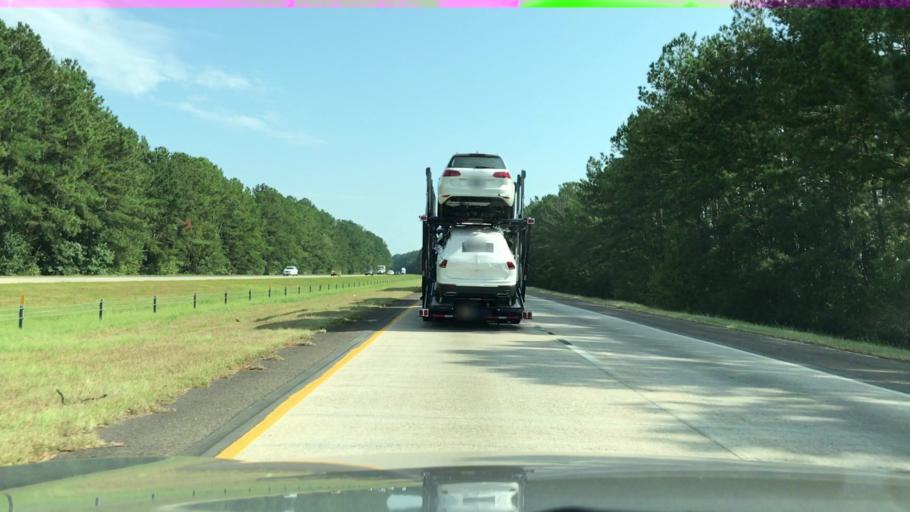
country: US
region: South Carolina
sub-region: Colleton County
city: Walterboro
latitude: 32.8166
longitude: -80.7589
